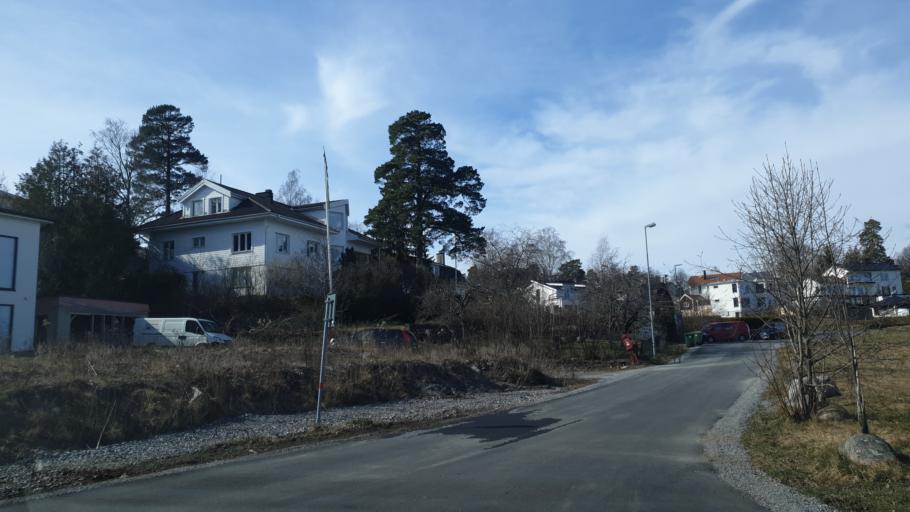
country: SE
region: Stockholm
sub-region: Sollentuna Kommun
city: Sollentuna
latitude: 59.4195
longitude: 17.9833
